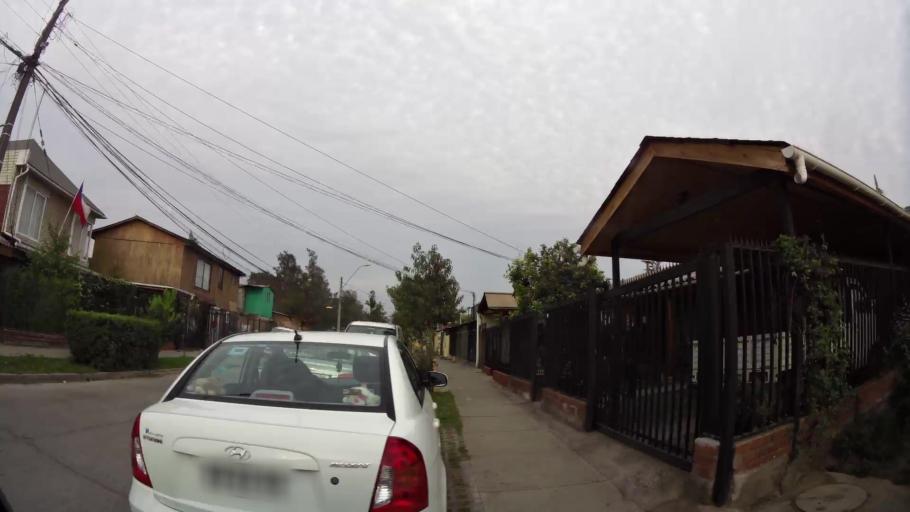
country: CL
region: Santiago Metropolitan
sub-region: Provincia de Santiago
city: Lo Prado
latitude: -33.5263
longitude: -70.7739
